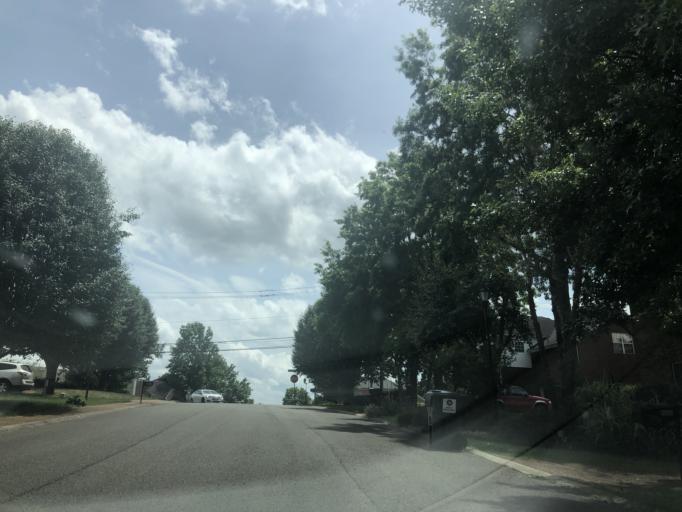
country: US
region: Tennessee
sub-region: Davidson County
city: Belle Meade
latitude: 36.0554
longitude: -86.9516
